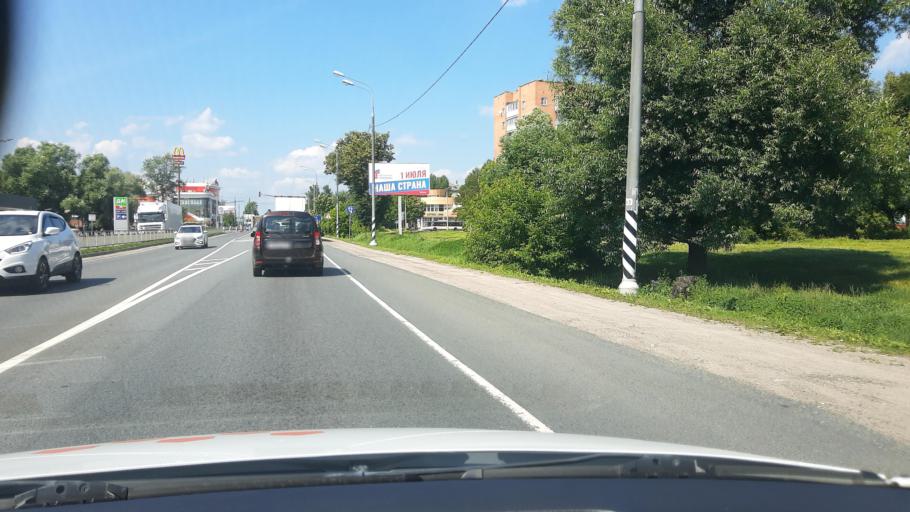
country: RU
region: Moskovskaya
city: Elektrostal'
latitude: 55.7676
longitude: 38.4352
